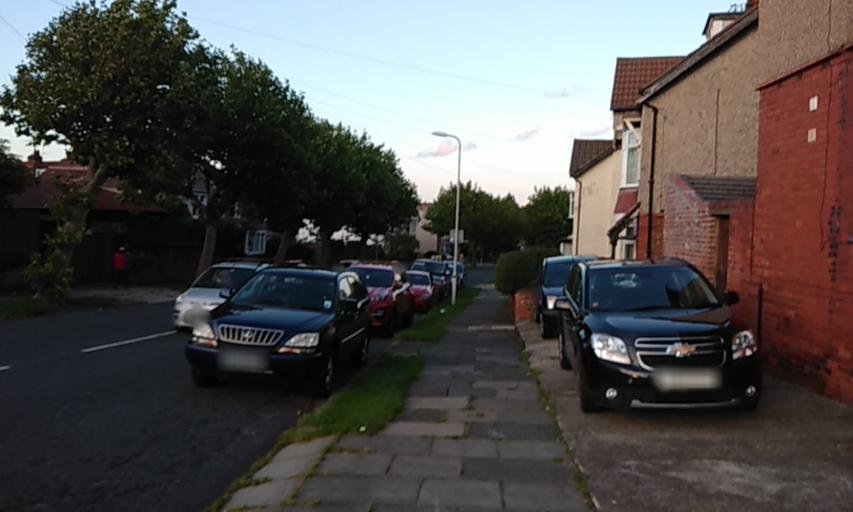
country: GB
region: England
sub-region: Metropolitan Borough of Wirral
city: Wallasey
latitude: 53.4221
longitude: -3.0596
